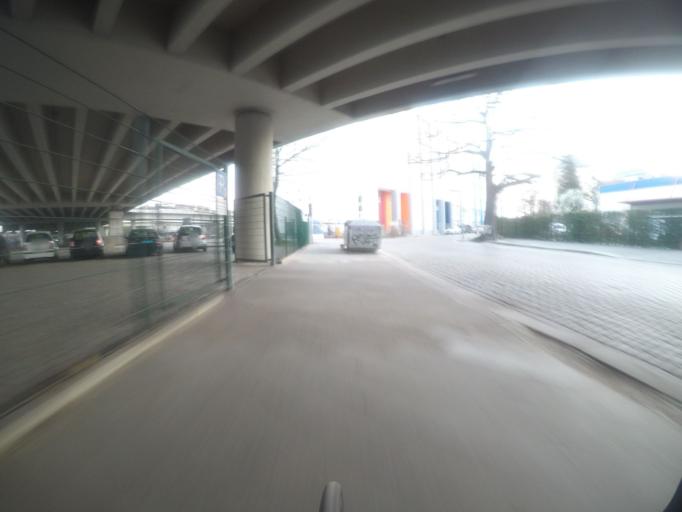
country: DE
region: Berlin
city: Steglitz Bezirk
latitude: 52.4596
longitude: 13.3293
